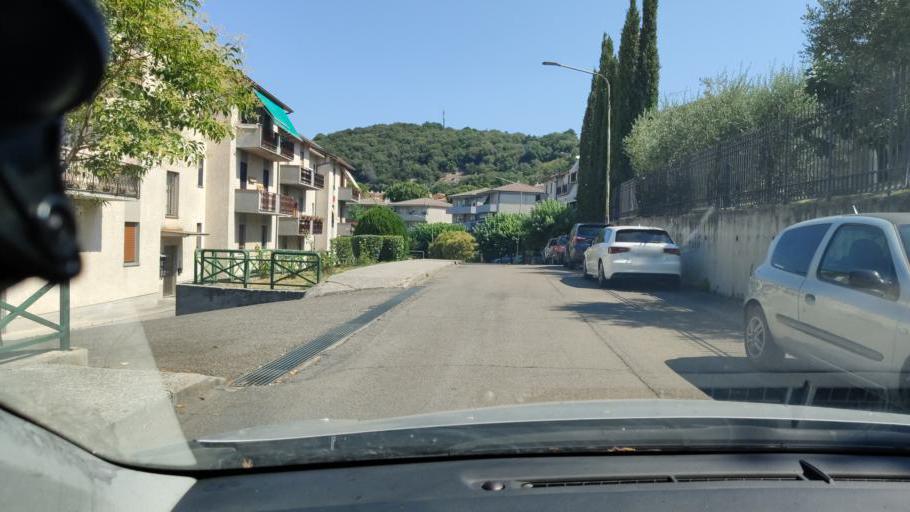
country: IT
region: Umbria
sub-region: Provincia di Terni
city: Fornole
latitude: 42.5414
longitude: 12.4541
